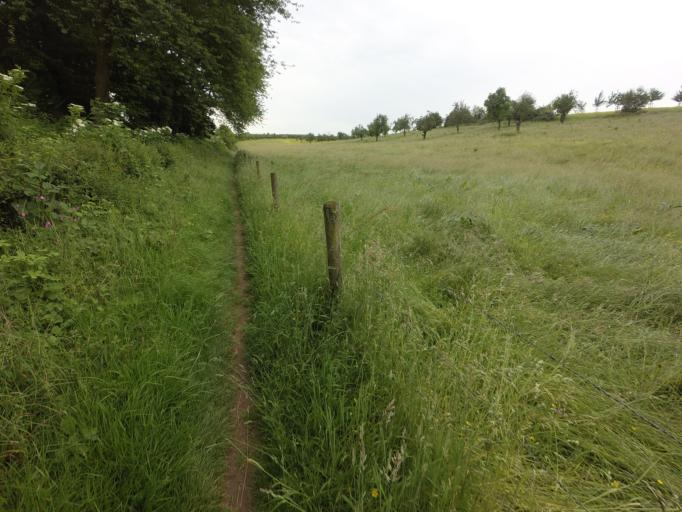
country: NL
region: Limburg
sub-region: Gemeente Voerendaal
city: Ubachsberg
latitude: 50.8516
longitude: 5.9676
